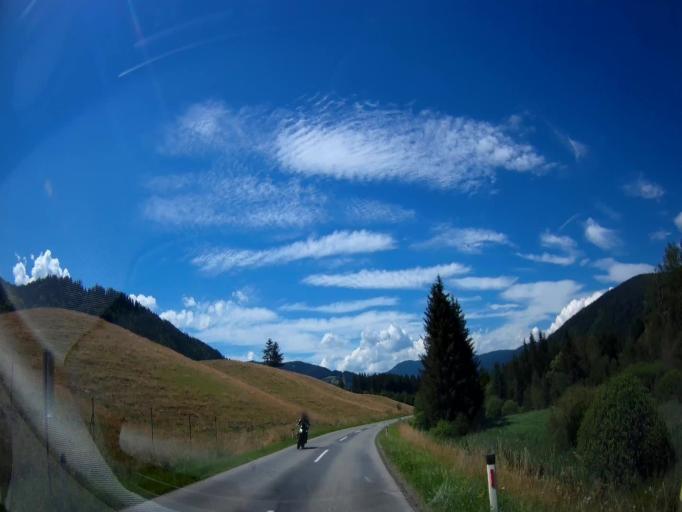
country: AT
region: Carinthia
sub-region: Politischer Bezirk Sankt Veit an der Glan
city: Glodnitz
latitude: 46.8593
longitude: 14.1305
